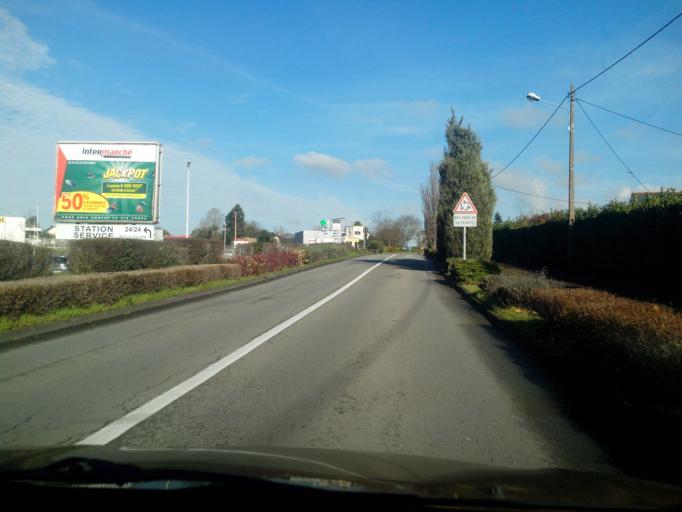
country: FR
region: Brittany
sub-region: Departement du Morbihan
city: Ploermel
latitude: 47.9233
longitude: -2.4020
